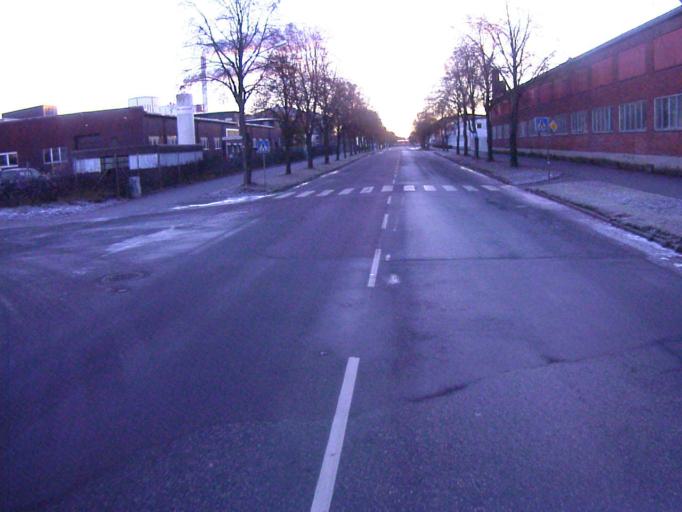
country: SE
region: Soedermanland
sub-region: Eskilstuna Kommun
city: Eskilstuna
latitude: 59.3810
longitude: 16.4857
